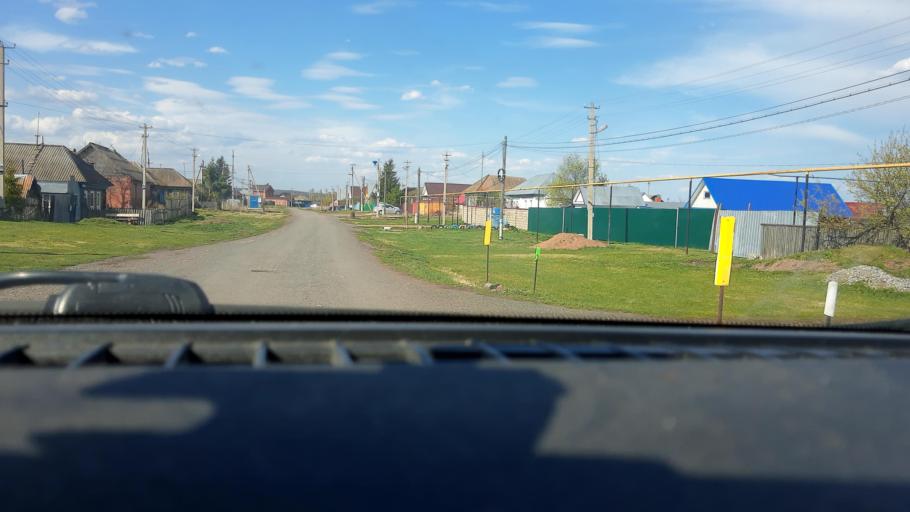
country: RU
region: Bashkortostan
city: Ufa
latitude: 54.5502
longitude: 55.9513
